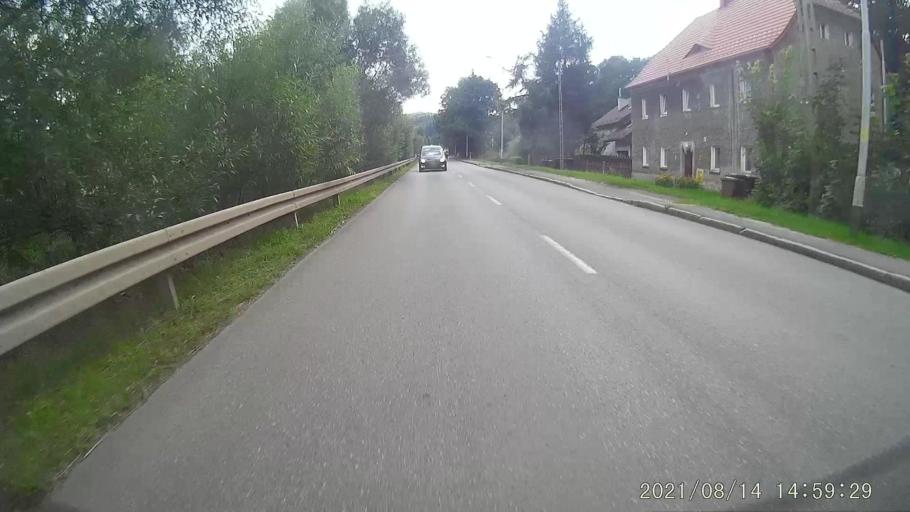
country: PL
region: Lower Silesian Voivodeship
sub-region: Powiat walbrzyski
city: Jedlina-Zdroj
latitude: 50.7108
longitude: 16.3616
